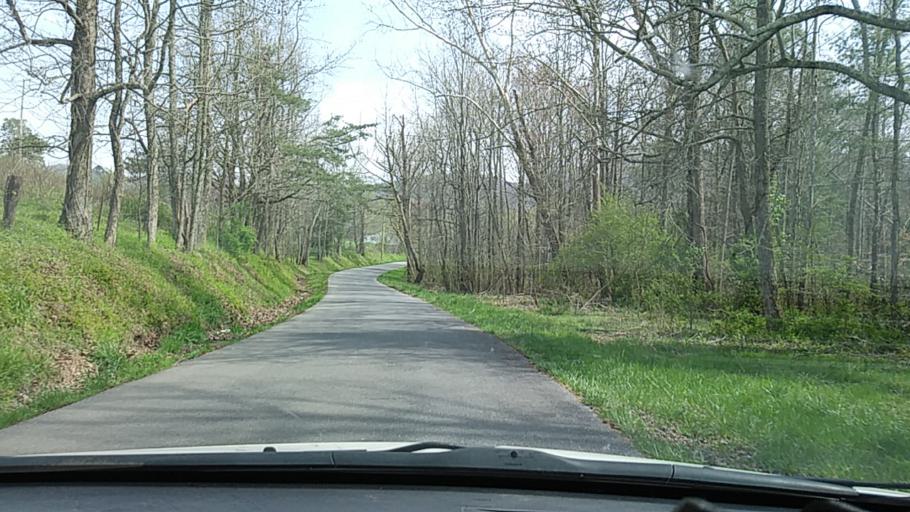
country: US
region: Tennessee
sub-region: Greene County
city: Tusculum
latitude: 36.0963
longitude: -82.7082
